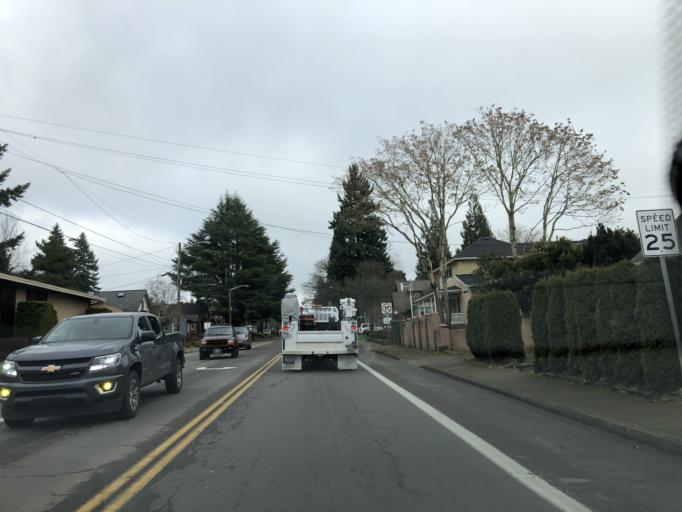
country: US
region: Washington
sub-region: Clark County
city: Vancouver
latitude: 45.6401
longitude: -122.6701
